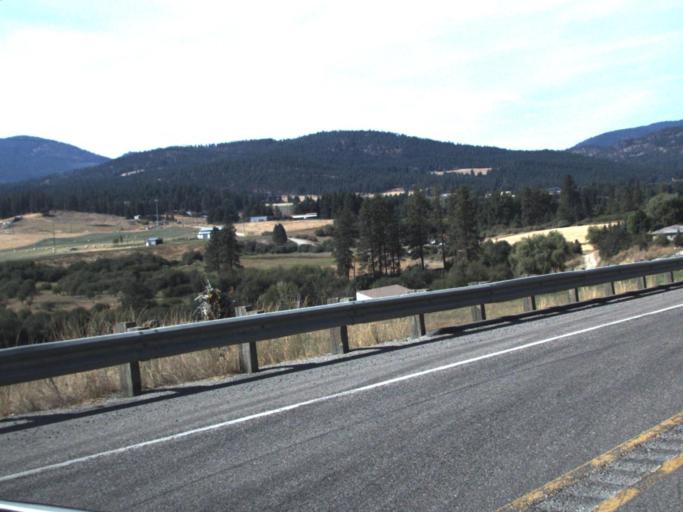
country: US
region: Washington
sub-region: Stevens County
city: Chewelah
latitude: 48.3099
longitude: -117.7880
